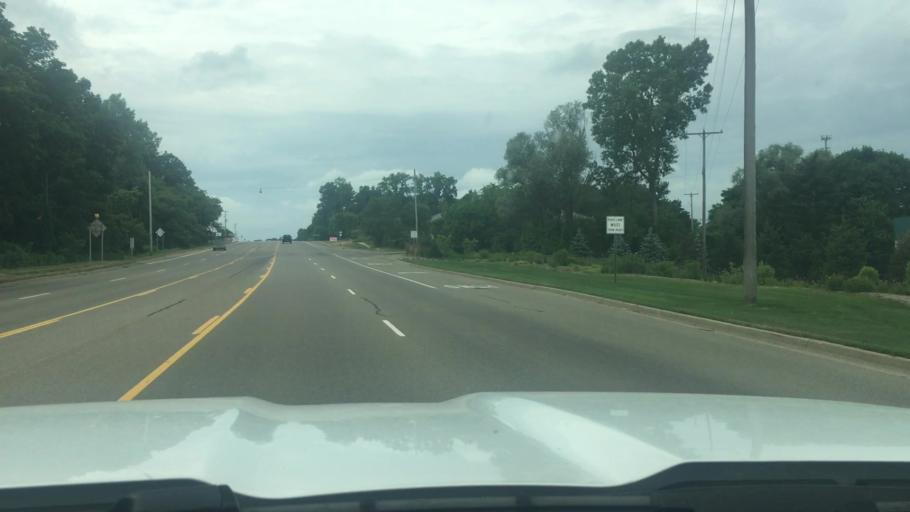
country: US
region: Michigan
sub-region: Kent County
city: Forest Hills
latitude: 42.9605
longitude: -85.4998
